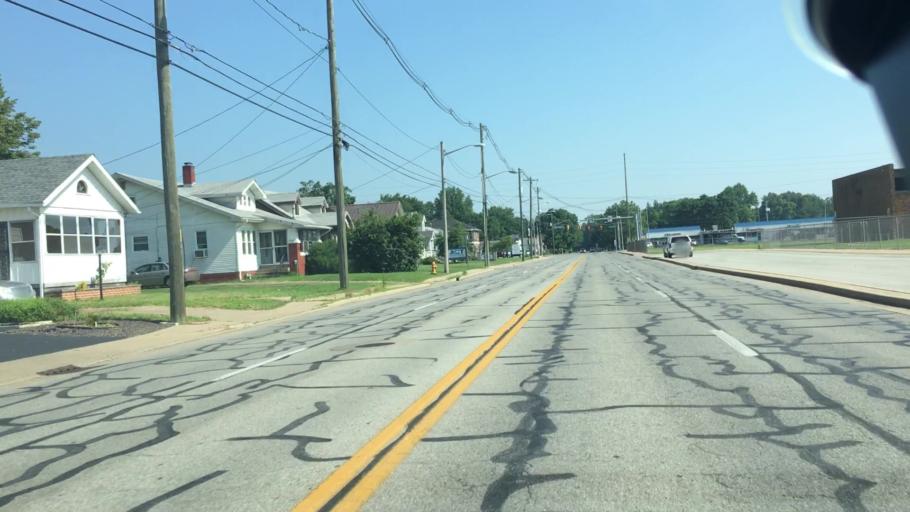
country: US
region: Indiana
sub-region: Vanderburgh County
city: Evansville
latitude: 37.9898
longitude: -87.5292
